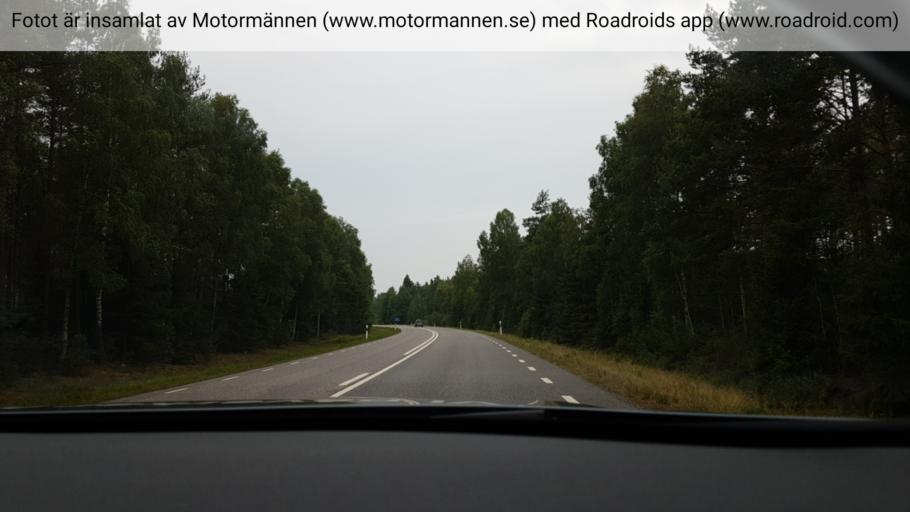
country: SE
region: Joenkoeping
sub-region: Varnamo Kommun
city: Bor
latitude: 57.2776
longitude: 14.2448
